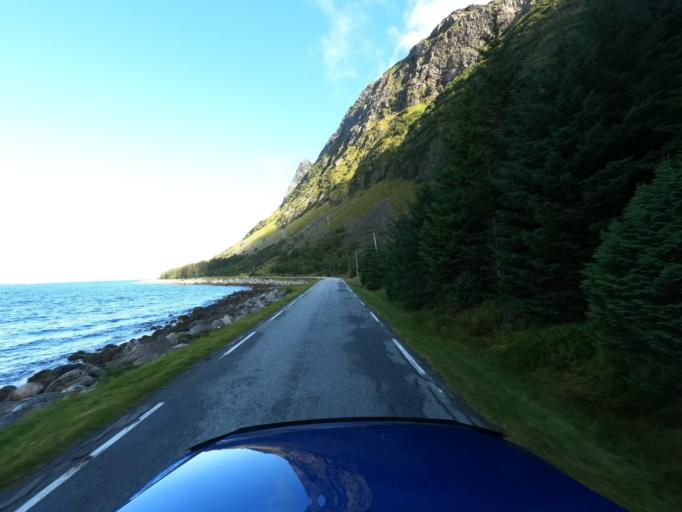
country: NO
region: Nordland
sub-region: Vagan
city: Kabelvag
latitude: 68.3099
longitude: 14.3127
